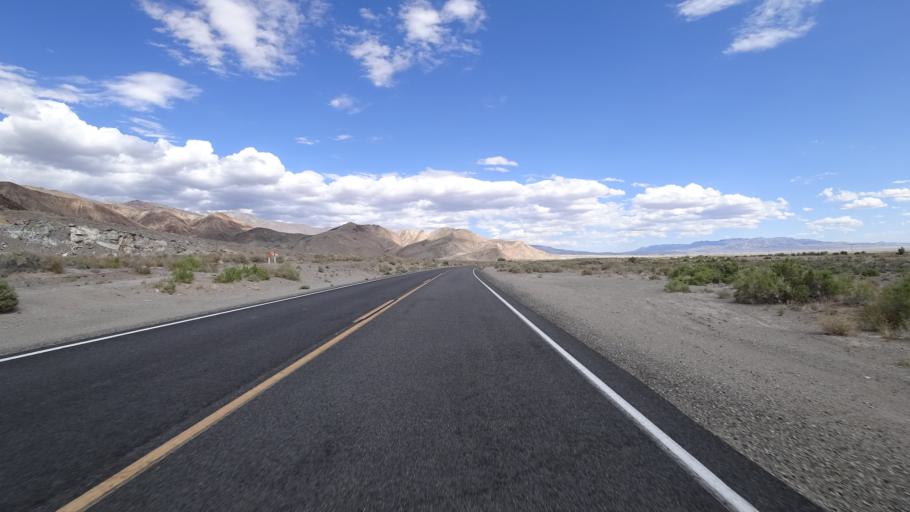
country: US
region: California
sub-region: Inyo County
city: Lone Pine
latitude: 36.5294
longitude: -117.9119
